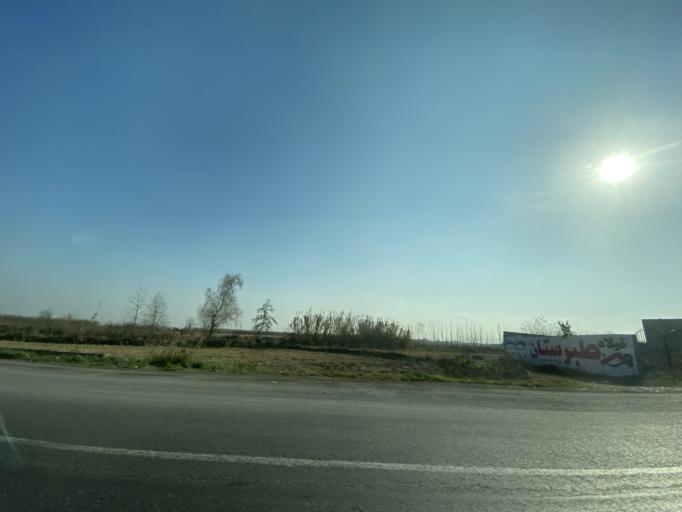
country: IR
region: Mazandaran
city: Amol
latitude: 36.4952
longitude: 52.5095
